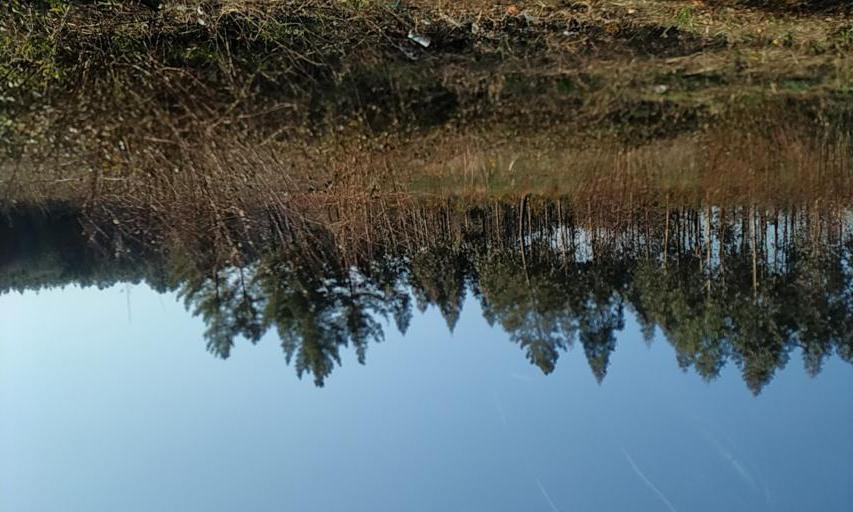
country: ES
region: Galicia
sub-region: Provincia de Lugo
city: Corgo
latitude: 42.9379
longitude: -7.4144
